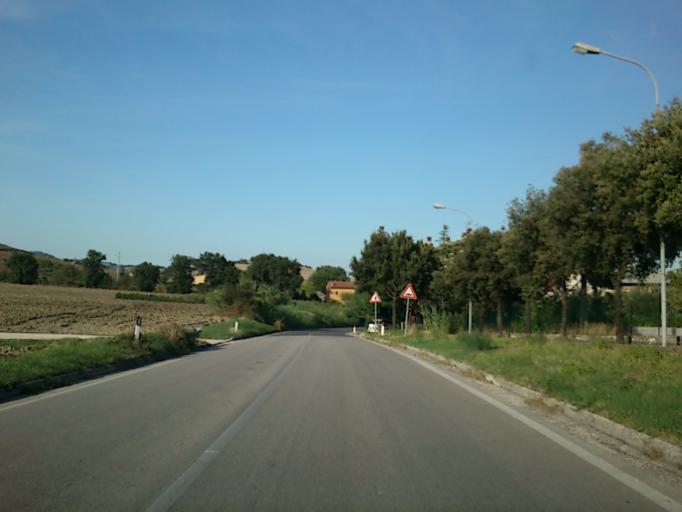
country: IT
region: The Marches
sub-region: Provincia di Pesaro e Urbino
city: Montefelcino
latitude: 43.7088
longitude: 12.8450
